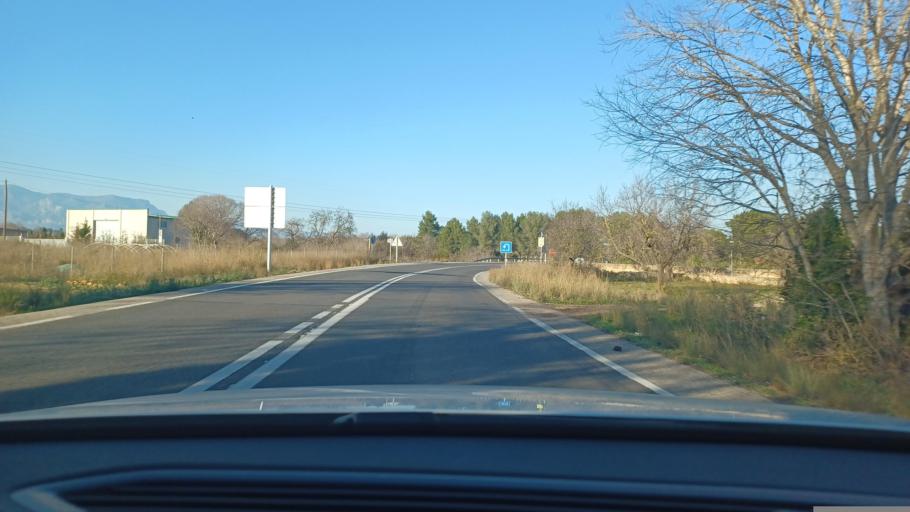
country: ES
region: Catalonia
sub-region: Provincia de Tarragona
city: Santa Barbara
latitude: 40.6803
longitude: 0.4586
